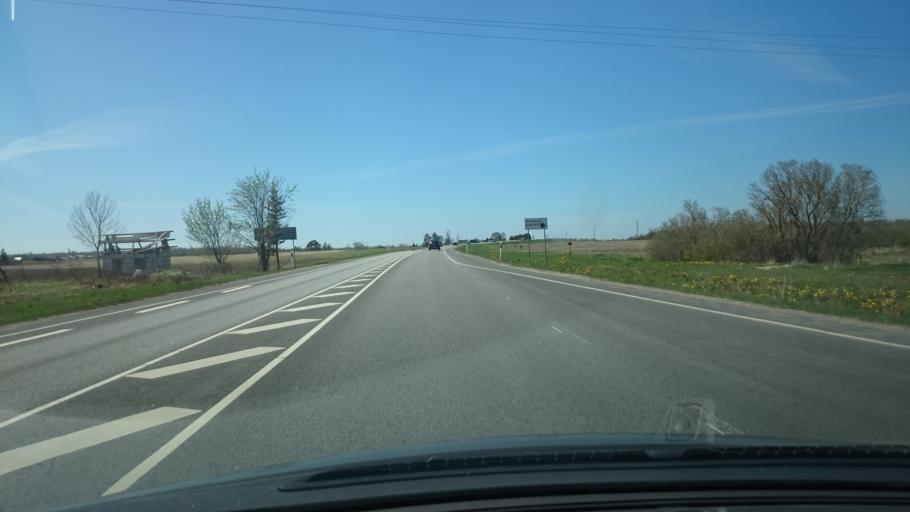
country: EE
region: Ida-Virumaa
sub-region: Narva-Joesuu linn
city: Narva-Joesuu
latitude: 59.4014
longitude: 28.0621
